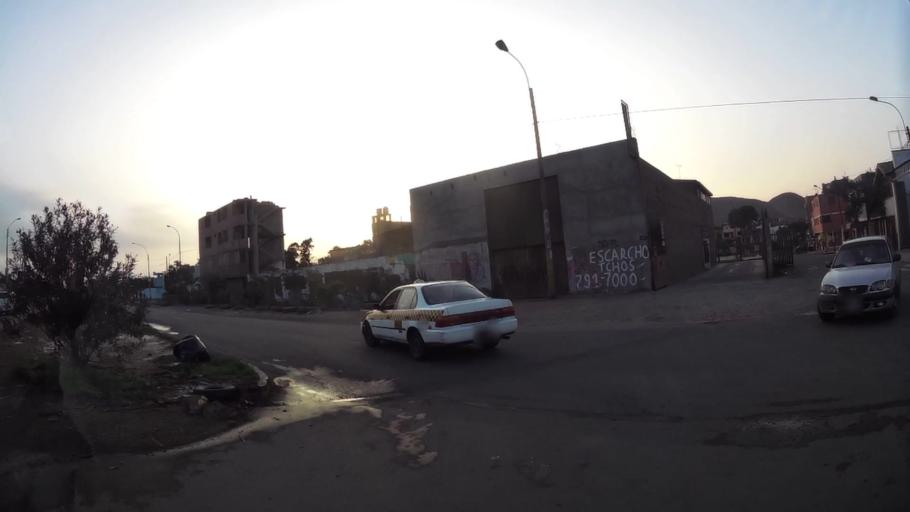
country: PE
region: Lima
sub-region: Lima
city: Independencia
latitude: -12.0091
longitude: -77.0659
